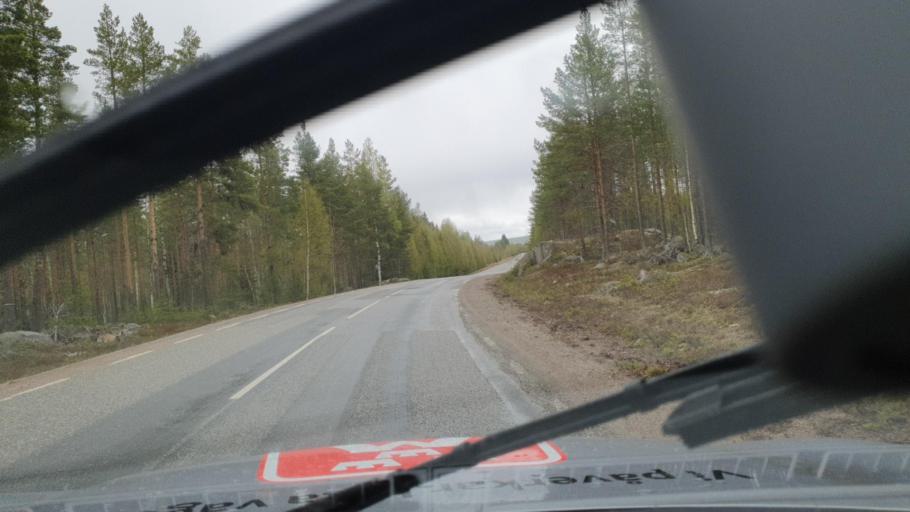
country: SE
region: Vaesterbotten
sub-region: Asele Kommun
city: Asele
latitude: 63.7051
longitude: 17.1501
